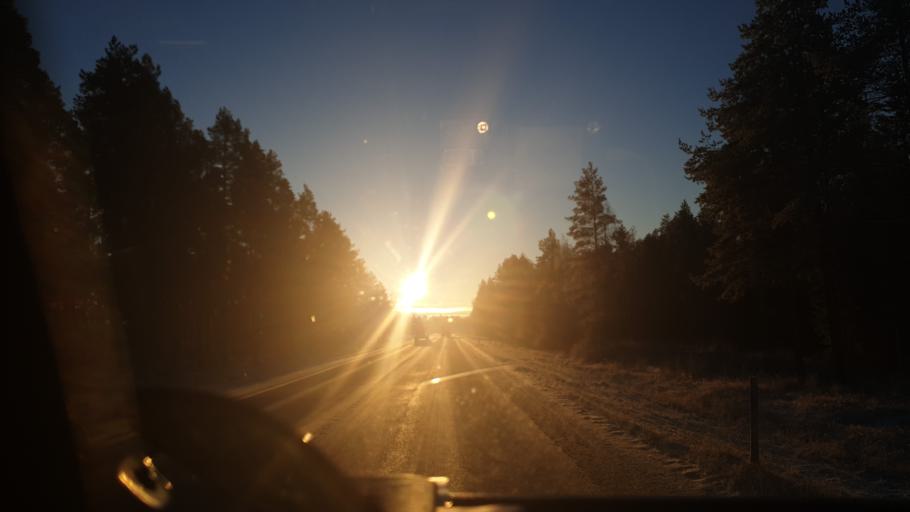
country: FI
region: Northern Ostrobothnia
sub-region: Ylivieska
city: Kalajoki
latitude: 64.2881
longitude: 23.9457
